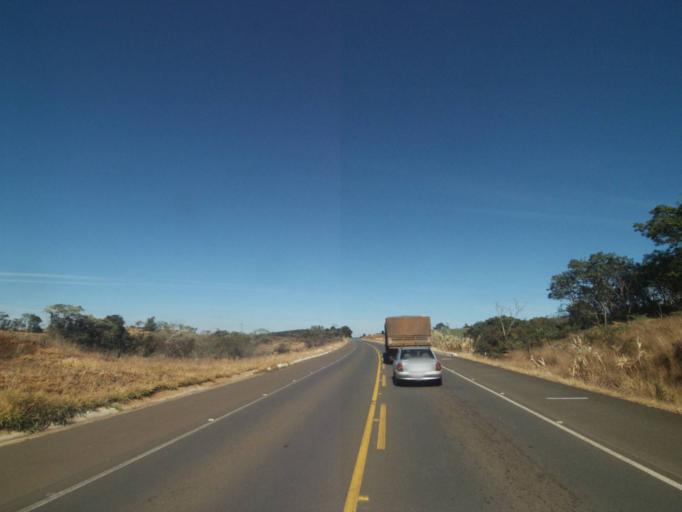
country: BR
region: Parana
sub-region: Tibagi
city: Tibagi
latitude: -24.7259
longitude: -50.4516
